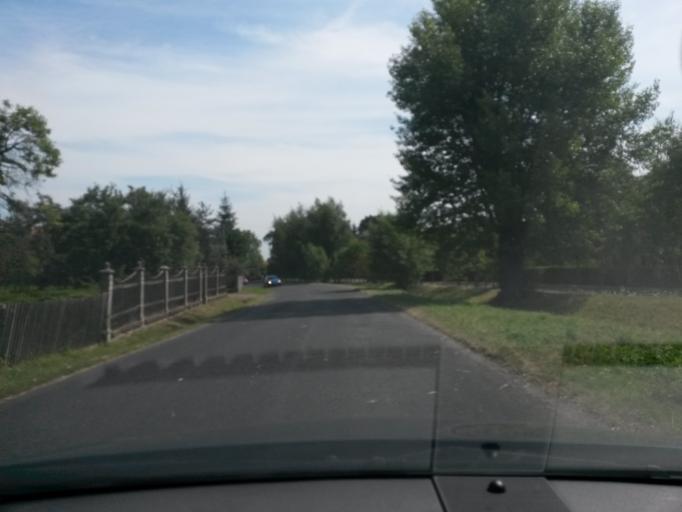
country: PL
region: Lower Silesian Voivodeship
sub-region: Powiat jaworski
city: Paszowice
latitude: 51.0131
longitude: 16.1571
